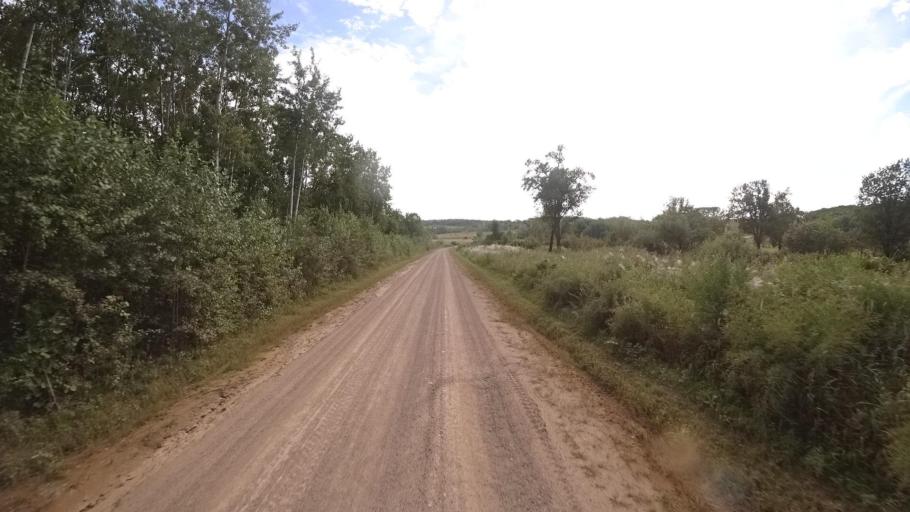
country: RU
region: Primorskiy
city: Dostoyevka
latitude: 44.3706
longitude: 133.5255
